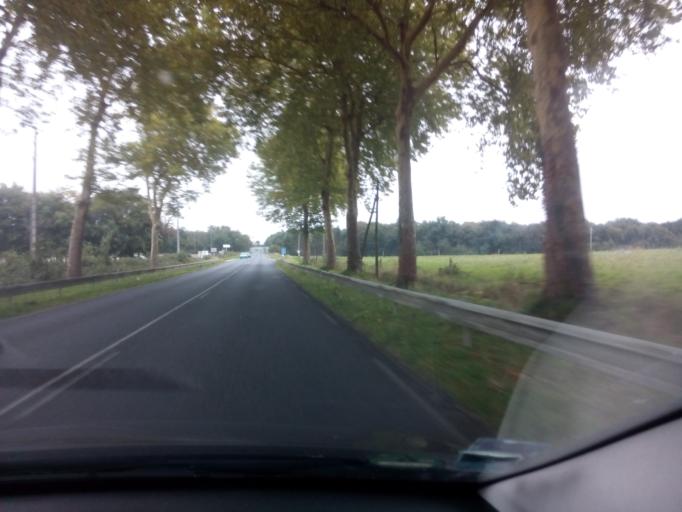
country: FR
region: Pays de la Loire
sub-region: Departement de Maine-et-Loire
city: Seiches-sur-le-Loir
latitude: 47.5693
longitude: -0.3368
